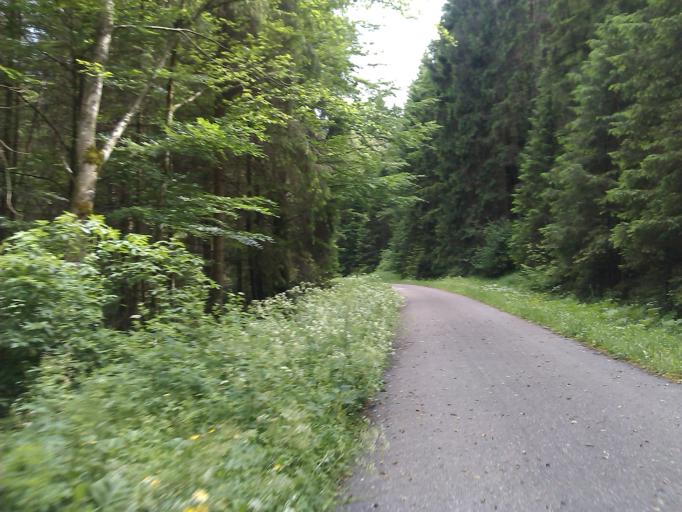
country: DE
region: Bavaria
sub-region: Swabia
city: Stotten am Auerberg
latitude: 47.6965
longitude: 10.7001
